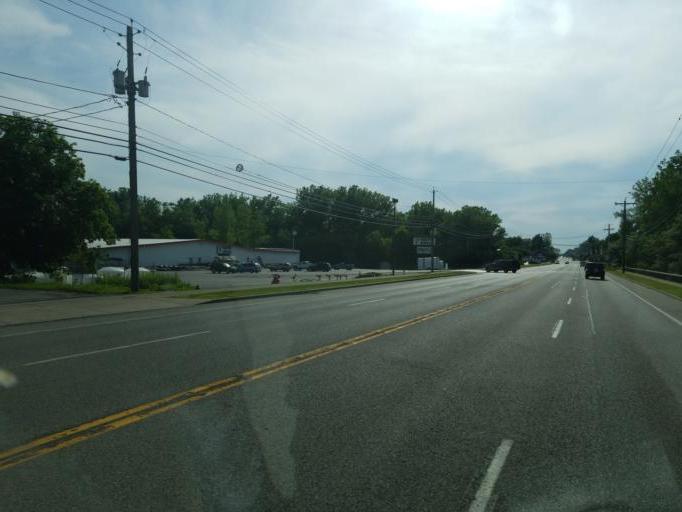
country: US
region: New York
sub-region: Genesee County
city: Batavia
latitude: 42.9930
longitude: -78.1515
